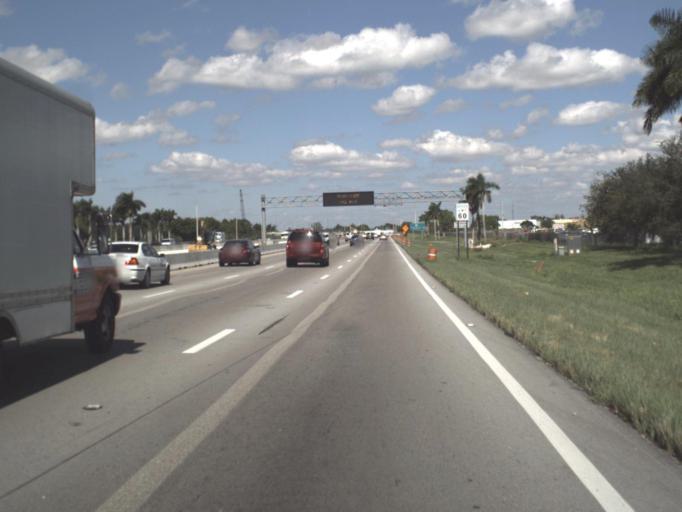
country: US
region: Florida
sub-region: Miami-Dade County
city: South Miami Heights
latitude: 25.5868
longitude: -80.3676
